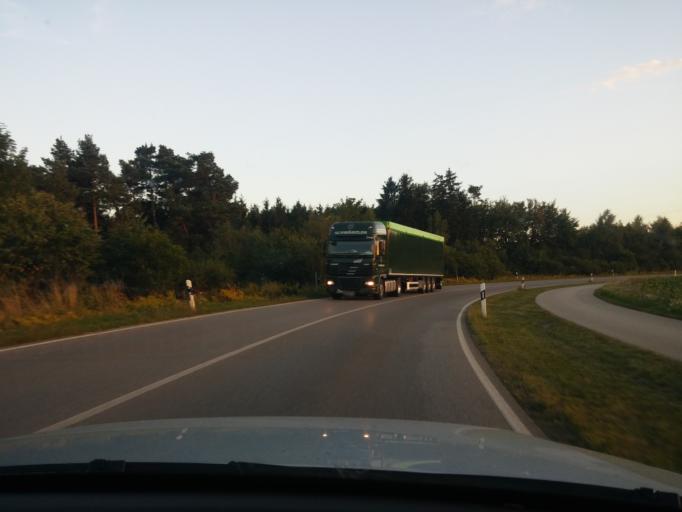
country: DE
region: Bavaria
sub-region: Upper Bavaria
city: Poing
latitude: 48.1633
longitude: 11.7935
